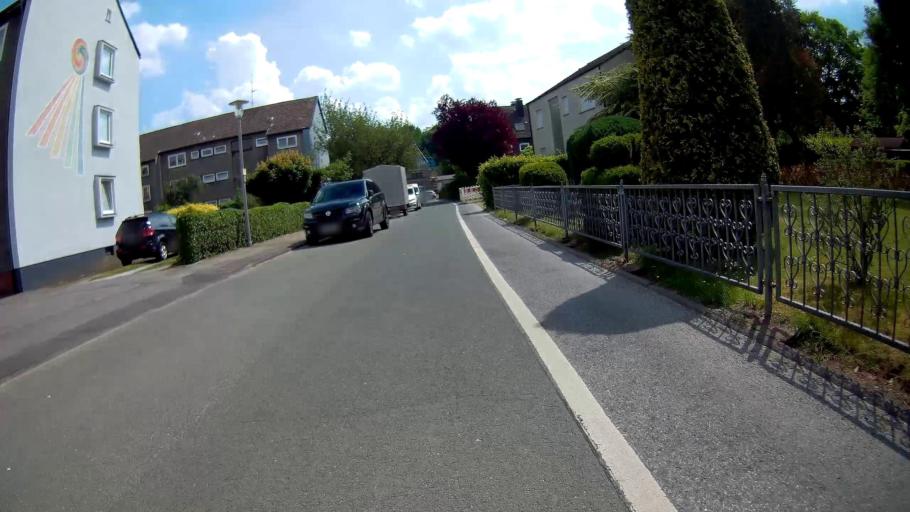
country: DE
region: North Rhine-Westphalia
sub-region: Regierungsbezirk Munster
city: Gladbeck
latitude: 51.5915
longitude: 6.9892
